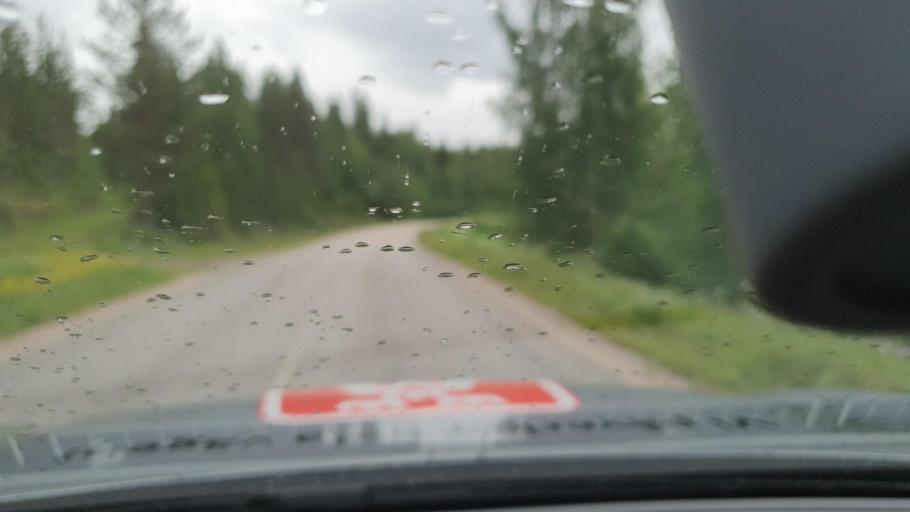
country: SE
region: Norrbotten
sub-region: Overkalix Kommun
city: OEverkalix
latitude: 66.4579
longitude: 22.7675
